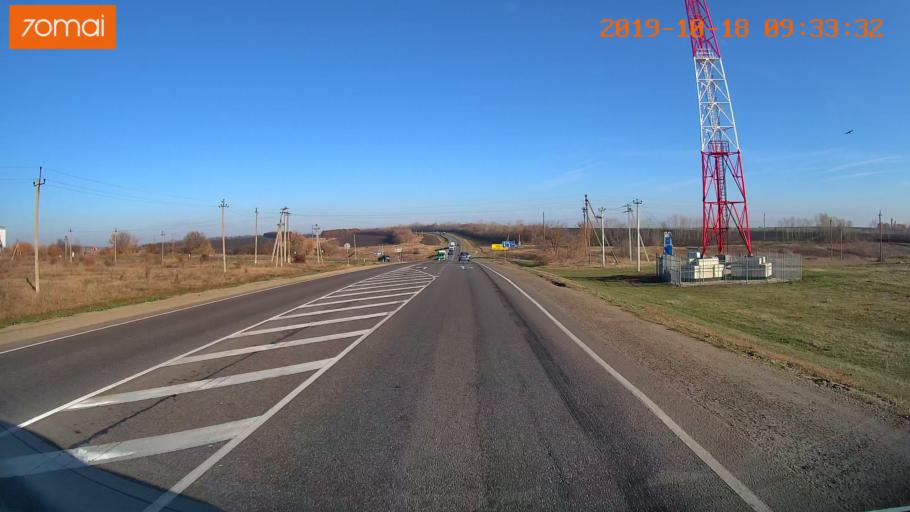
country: RU
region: Tula
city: Yefremov
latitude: 53.1679
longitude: 38.1512
